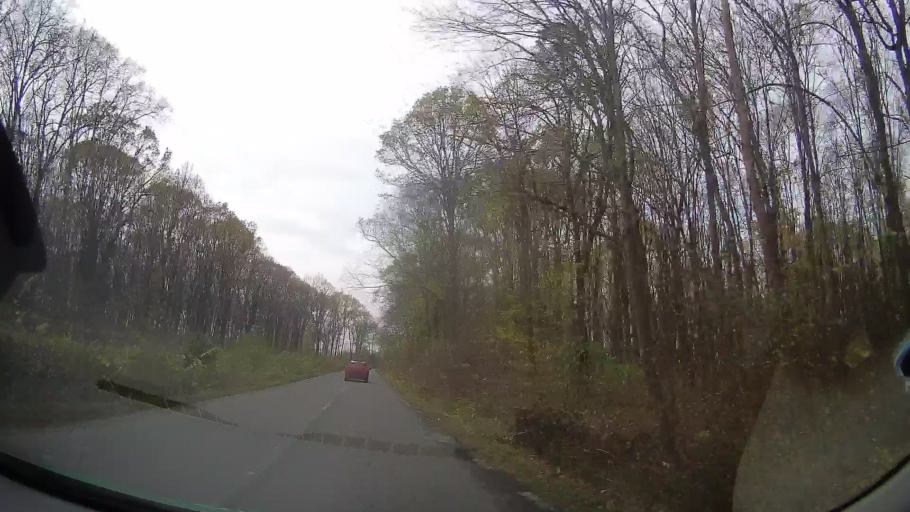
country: RO
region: Prahova
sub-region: Comuna Gorgota
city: Potigrafu
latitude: 44.7686
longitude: 26.1119
